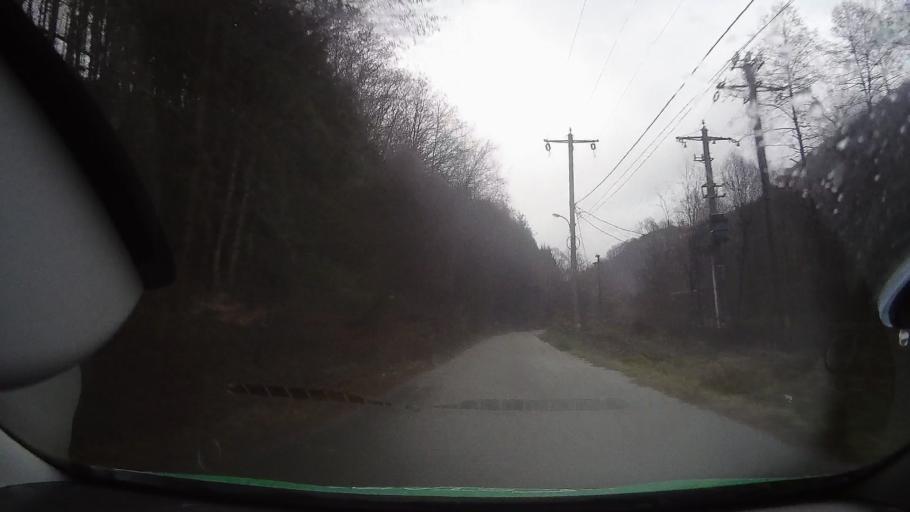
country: RO
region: Alba
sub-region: Comuna Avram Iancu
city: Avram Iancu
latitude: 46.2898
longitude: 22.7503
